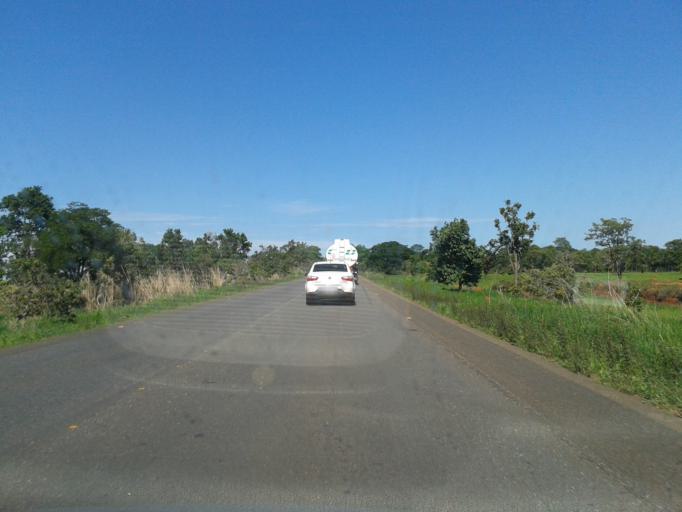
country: BR
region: Goias
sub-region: Bela Vista De Goias
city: Bela Vista de Goias
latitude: -17.0905
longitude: -48.8740
